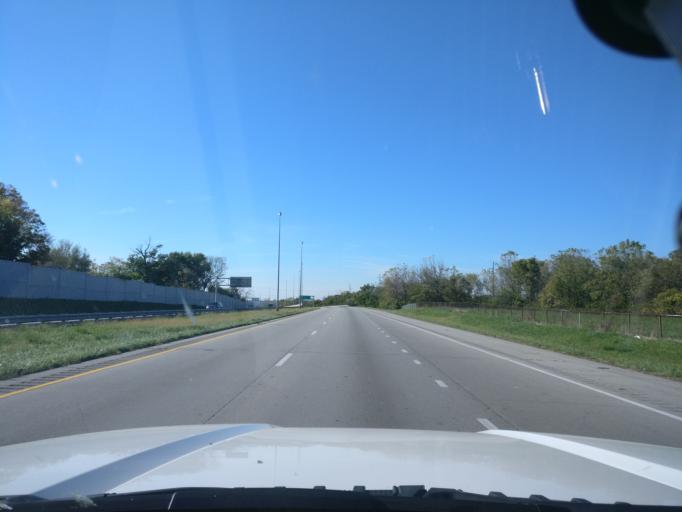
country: US
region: Ohio
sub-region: Montgomery County
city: Riverside
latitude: 39.7523
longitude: -84.1442
